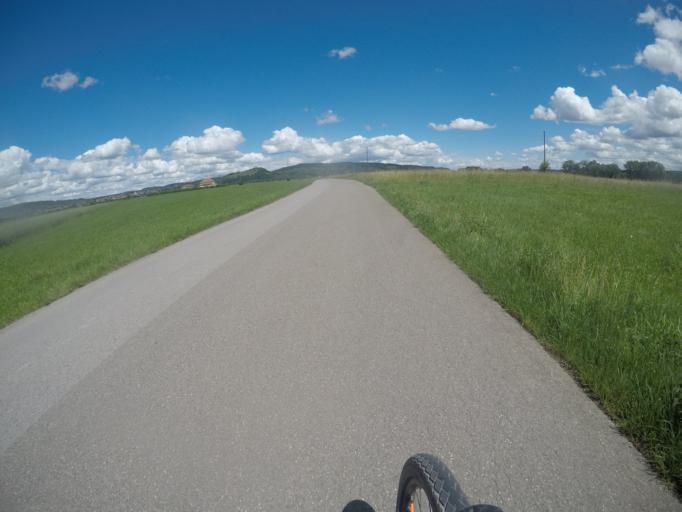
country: DE
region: Baden-Wuerttemberg
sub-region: Tuebingen Region
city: Rottenburg
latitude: 48.4830
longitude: 8.9655
